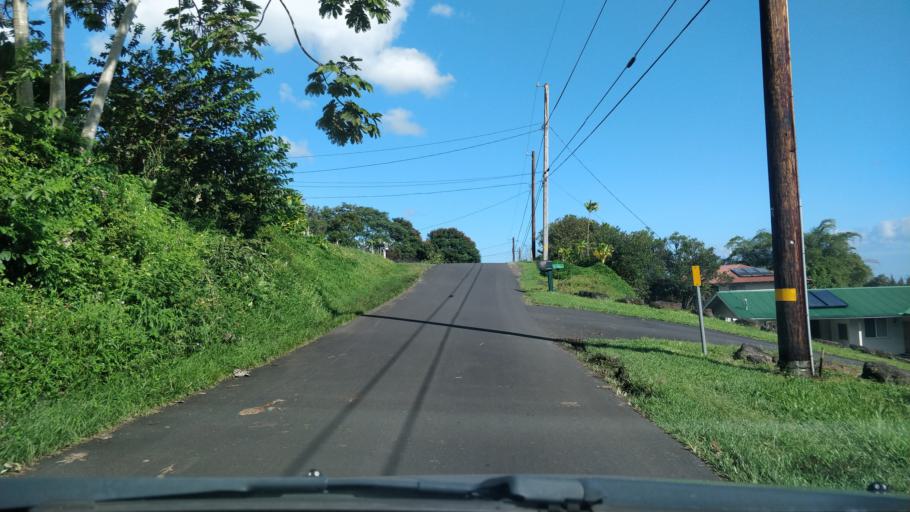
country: US
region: Hawaii
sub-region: Hawaii County
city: Hilo
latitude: 19.6612
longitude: -155.0992
